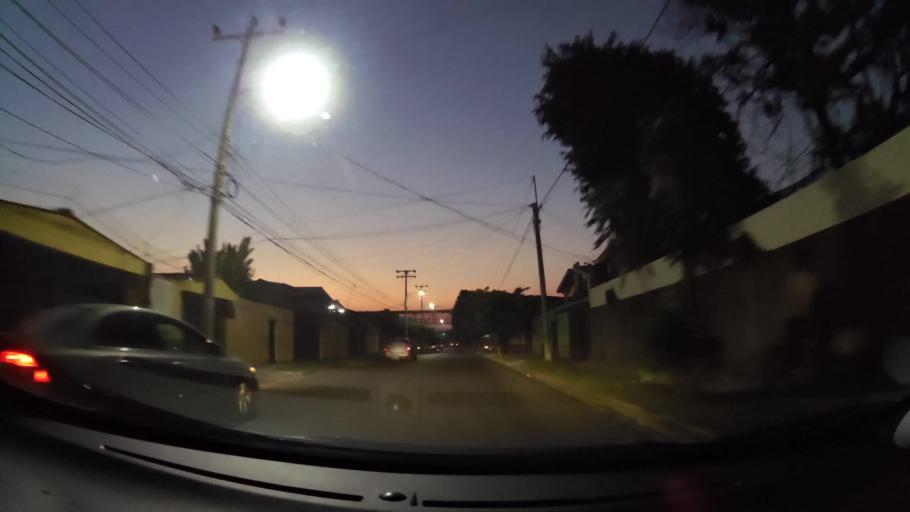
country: SV
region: La Libertad
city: Santa Tecla
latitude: 13.6798
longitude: -89.2861
